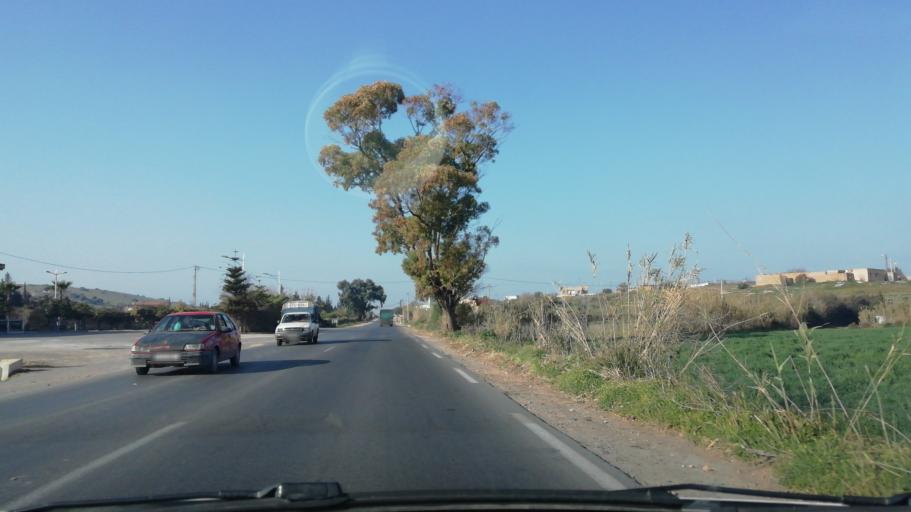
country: DZ
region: Mostaganem
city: Mostaganem
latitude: 35.7573
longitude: 0.2057
